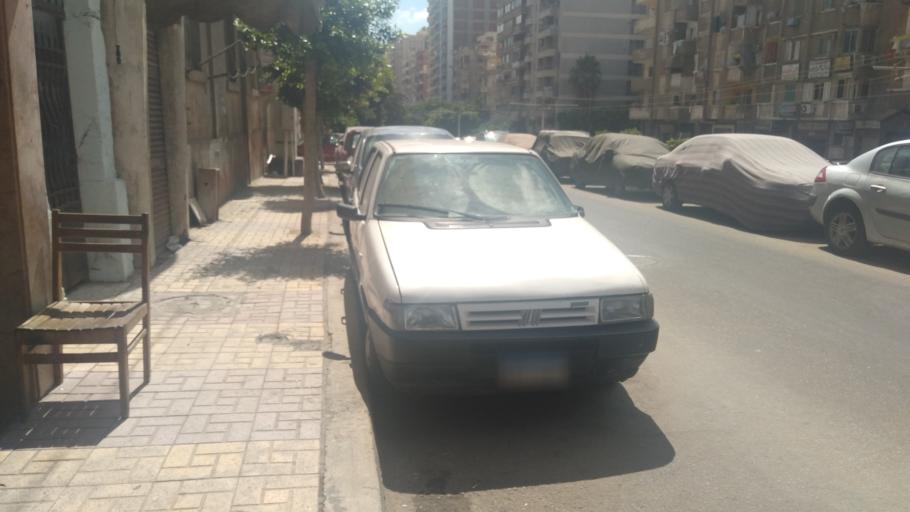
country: EG
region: Alexandria
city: Alexandria
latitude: 31.2201
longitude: 29.9359
